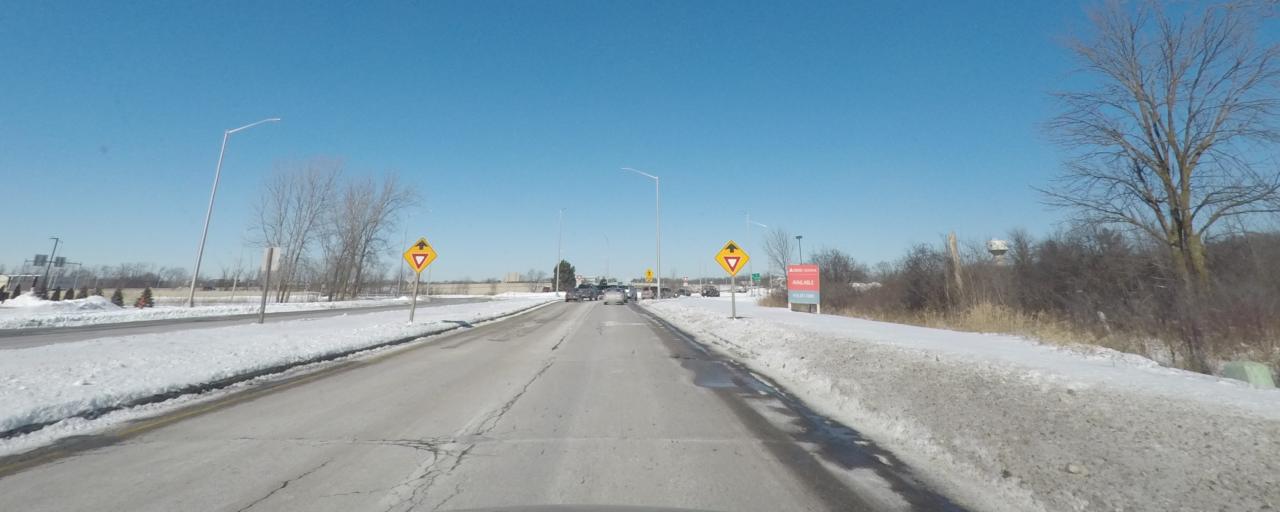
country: US
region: Wisconsin
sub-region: Waukesha County
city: New Berlin
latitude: 42.9481
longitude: -88.1089
